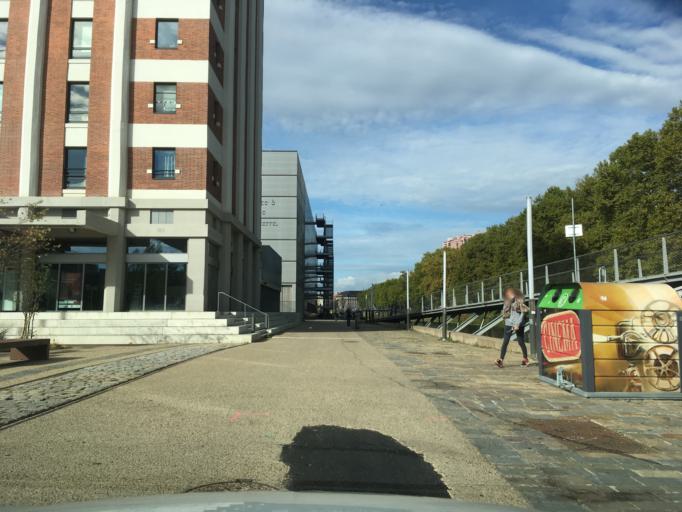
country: FR
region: Alsace
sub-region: Departement du Bas-Rhin
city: Strasbourg
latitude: 48.5744
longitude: 7.7626
